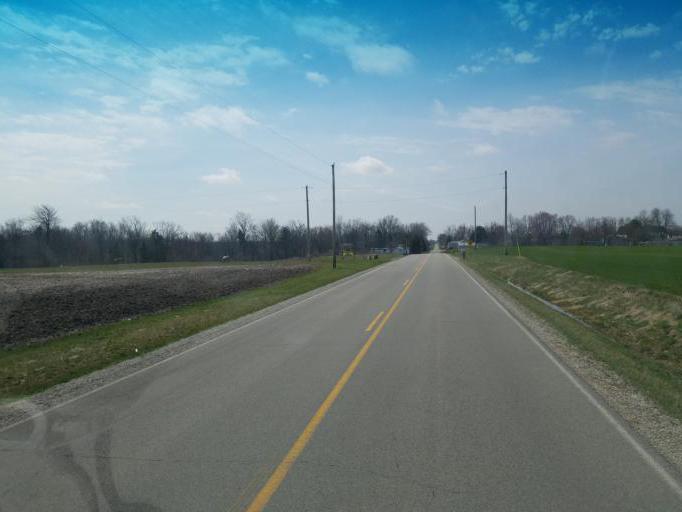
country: US
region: Ohio
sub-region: Crawford County
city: Bucyrus
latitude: 40.9311
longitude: -83.0933
